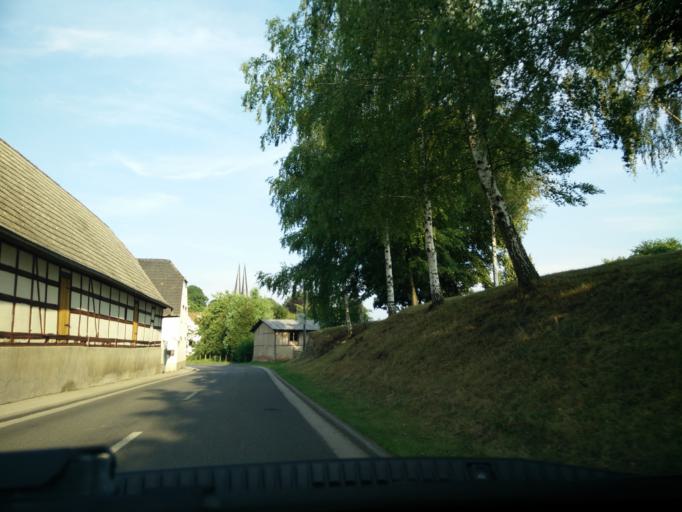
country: DE
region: Saxony
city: Frohburg
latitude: 51.0575
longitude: 12.5800
